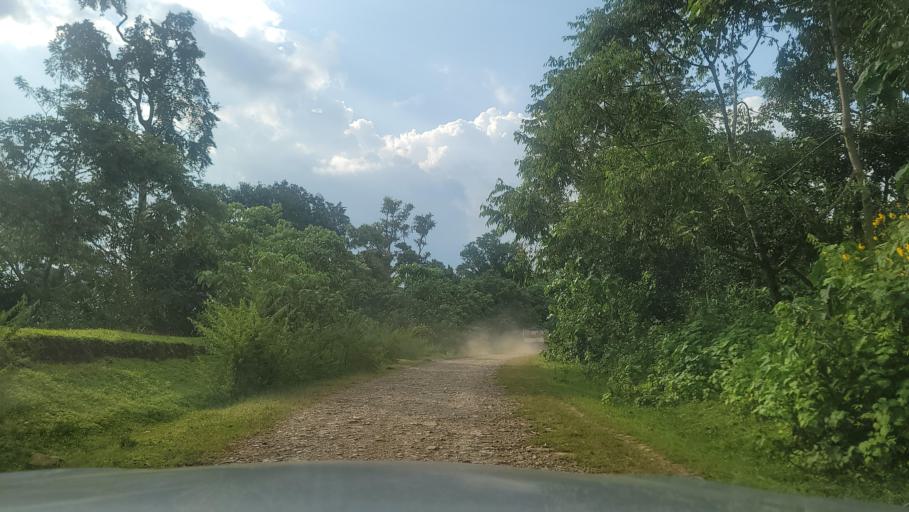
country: ET
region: Southern Nations, Nationalities, and People's Region
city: Bonga
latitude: 7.5769
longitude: 36.1615
